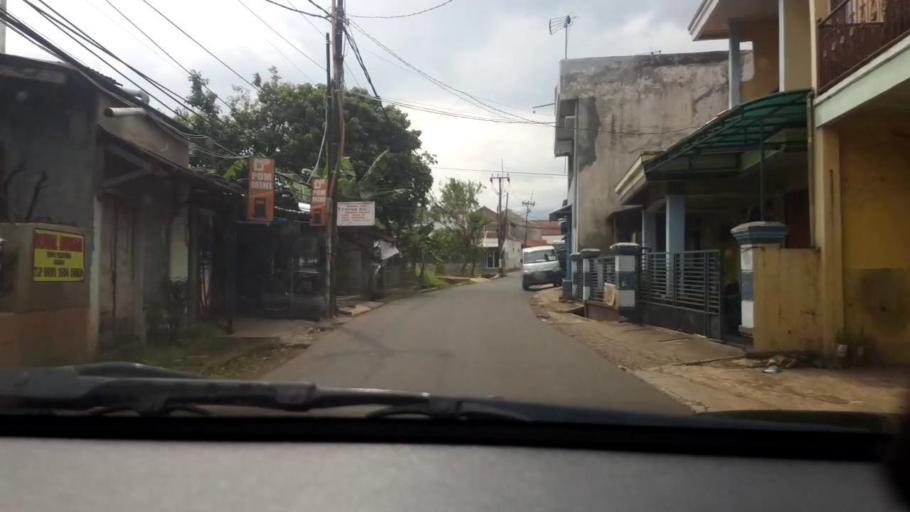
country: ID
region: West Java
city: Cileunyi
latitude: -6.9364
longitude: 107.7267
